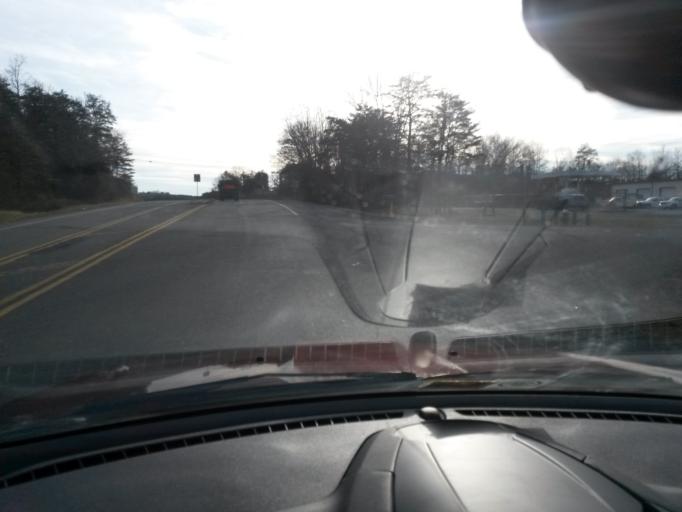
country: US
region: Virginia
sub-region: Alleghany County
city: Clifton Forge
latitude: 37.8375
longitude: -79.7598
